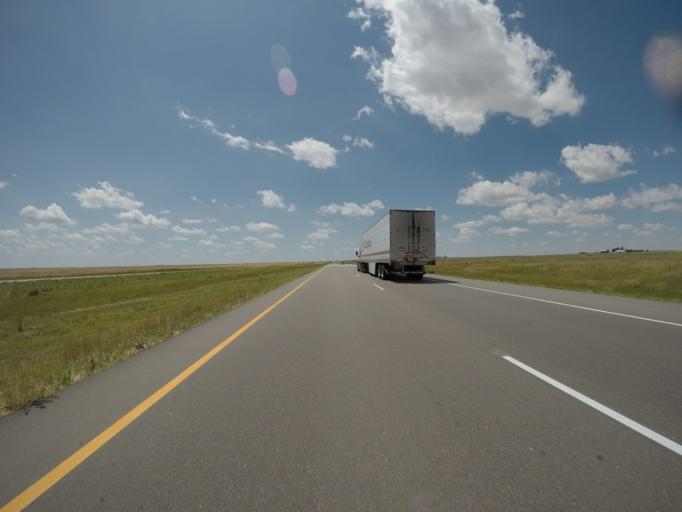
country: US
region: Colorado
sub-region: Kit Carson County
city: Burlington
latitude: 39.2941
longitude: -102.8356
